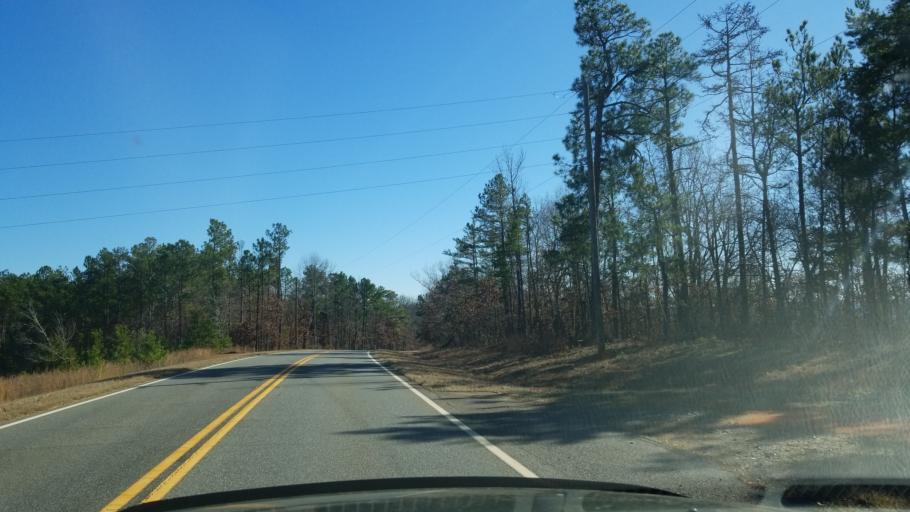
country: US
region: Georgia
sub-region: Talbot County
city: Sardis
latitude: 32.8464
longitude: -84.6940
